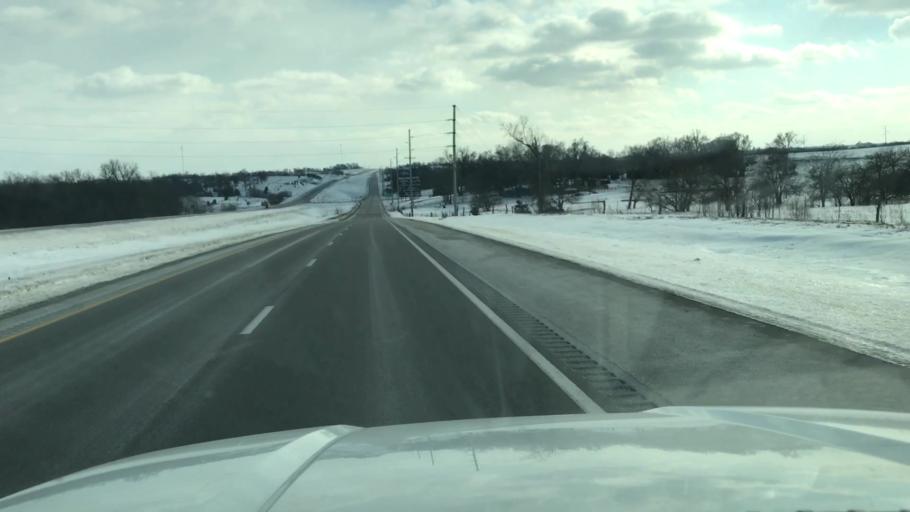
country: US
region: Missouri
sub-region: Nodaway County
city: Maryville
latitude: 40.2049
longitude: -94.8681
